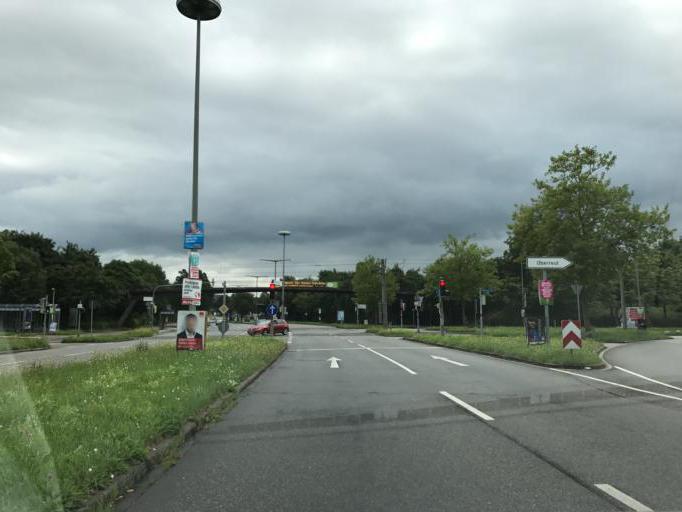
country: DE
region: Baden-Wuerttemberg
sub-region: Karlsruhe Region
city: Karlsruhe
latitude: 48.9927
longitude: 8.3678
